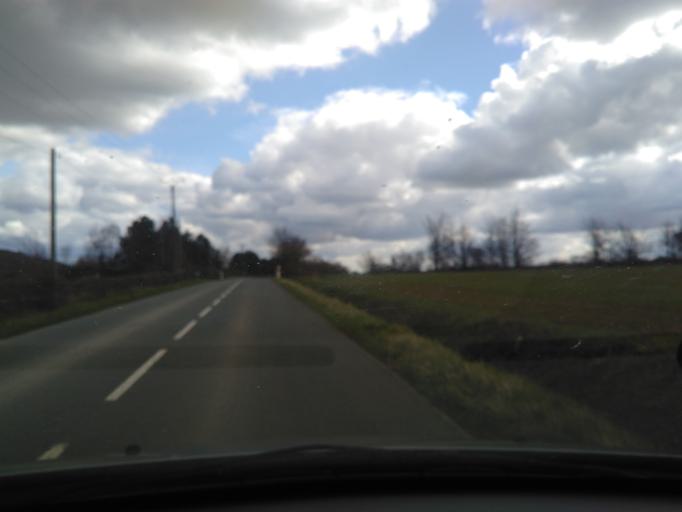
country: FR
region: Pays de la Loire
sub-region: Departement de la Vendee
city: Saint-Martin-des-Noyers
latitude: 46.7021
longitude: -1.1448
